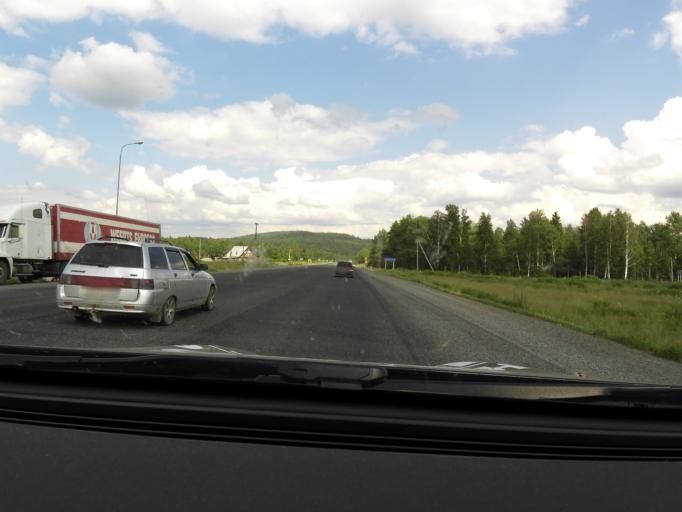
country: RU
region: Sverdlovsk
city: Arti
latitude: 56.7923
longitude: 58.6080
